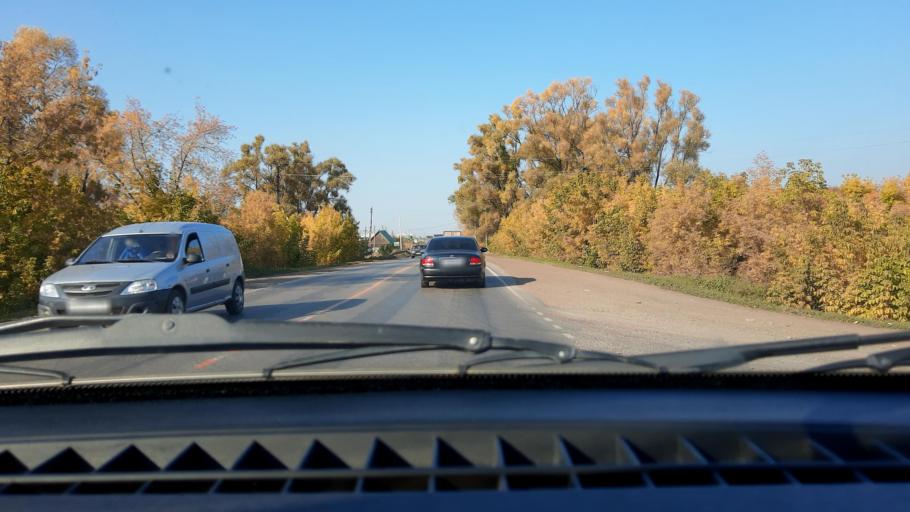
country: RU
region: Bashkortostan
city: Avdon
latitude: 54.7337
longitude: 55.8037
